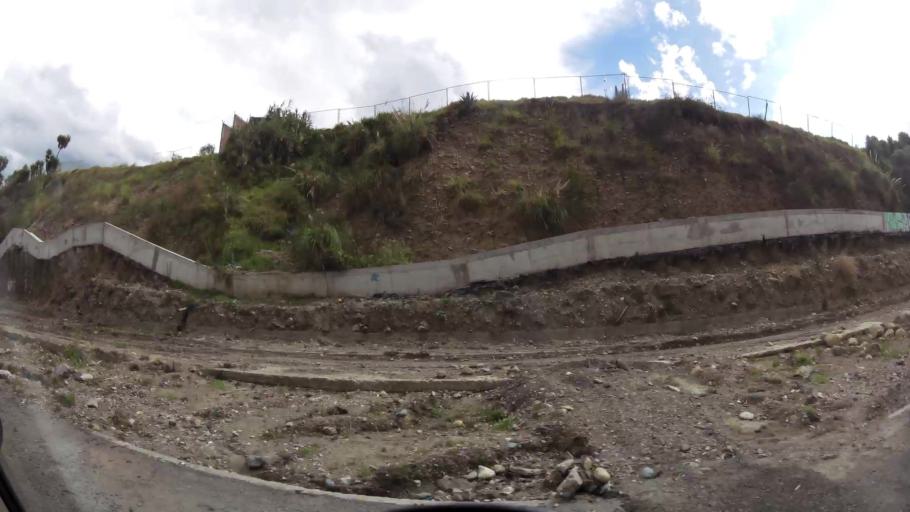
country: EC
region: Azuay
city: Cuenca
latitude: -2.8834
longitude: -78.9794
